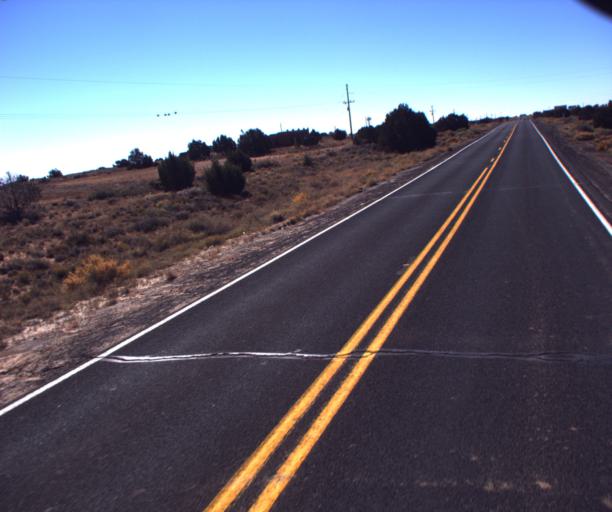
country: US
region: Arizona
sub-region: Navajo County
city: First Mesa
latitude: 35.8355
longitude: -110.5280
